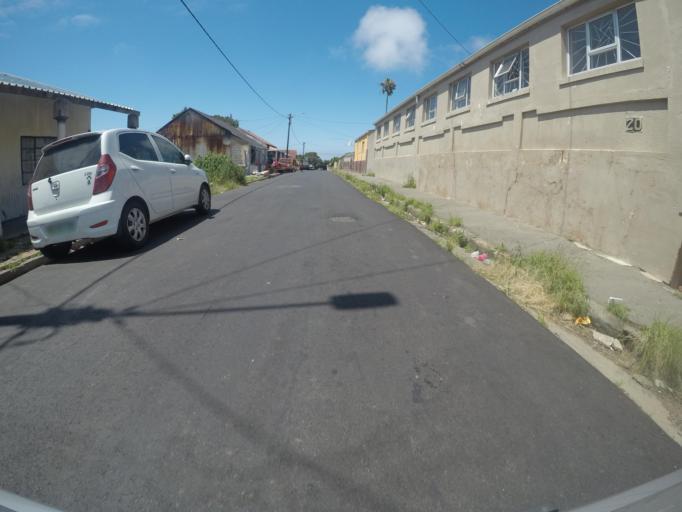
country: ZA
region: Eastern Cape
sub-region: Buffalo City Metropolitan Municipality
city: East London
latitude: -33.0005
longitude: 27.9108
